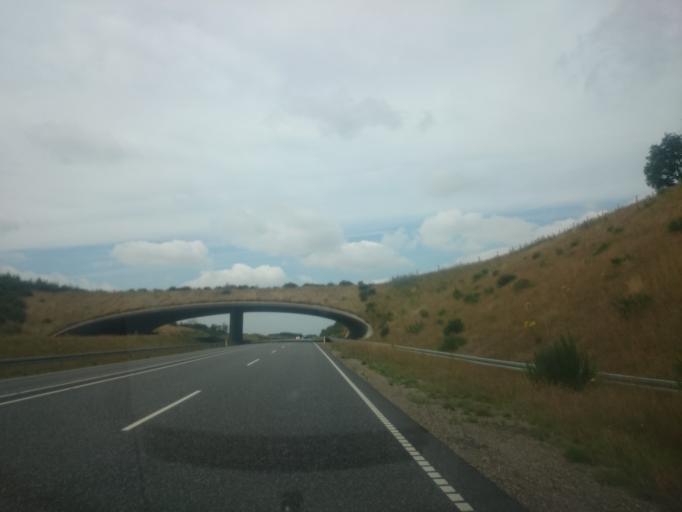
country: DK
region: South Denmark
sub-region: Vejle Kommune
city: Egtved
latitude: 55.7064
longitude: 9.2585
